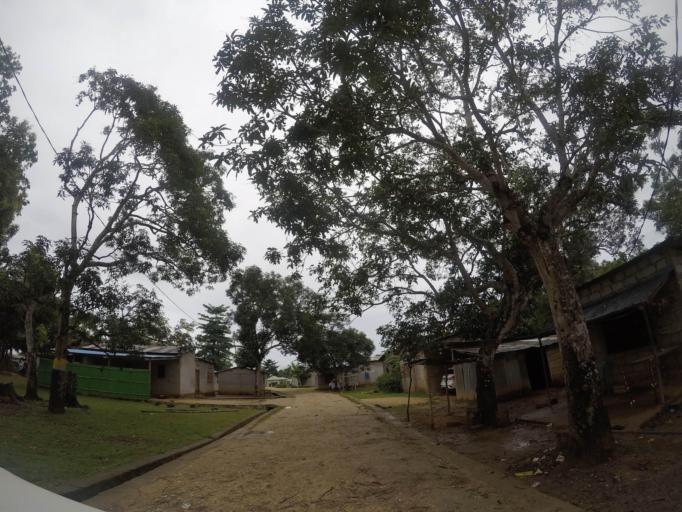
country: TL
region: Lautem
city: Lospalos
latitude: -8.5231
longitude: 127.0064
